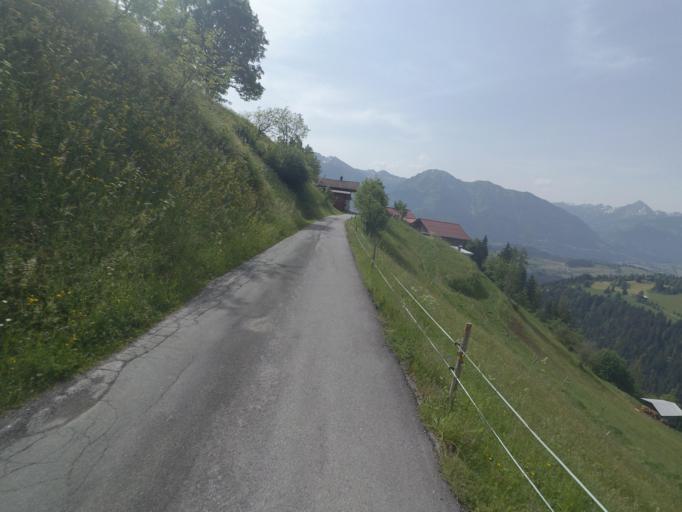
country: AT
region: Salzburg
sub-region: Politischer Bezirk Sankt Johann im Pongau
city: Muhlbach am Hochkonig
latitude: 47.3488
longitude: 13.1202
